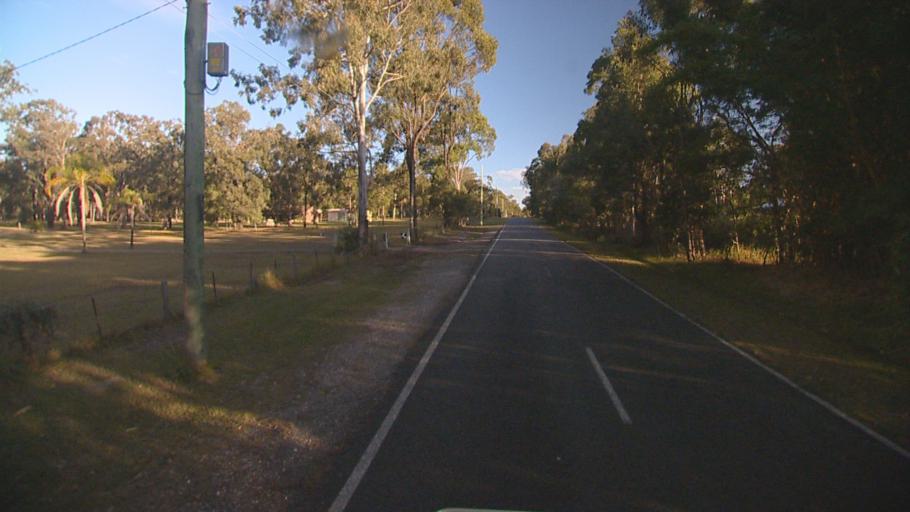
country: AU
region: Queensland
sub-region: Logan
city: Waterford West
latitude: -27.7246
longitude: 153.1414
